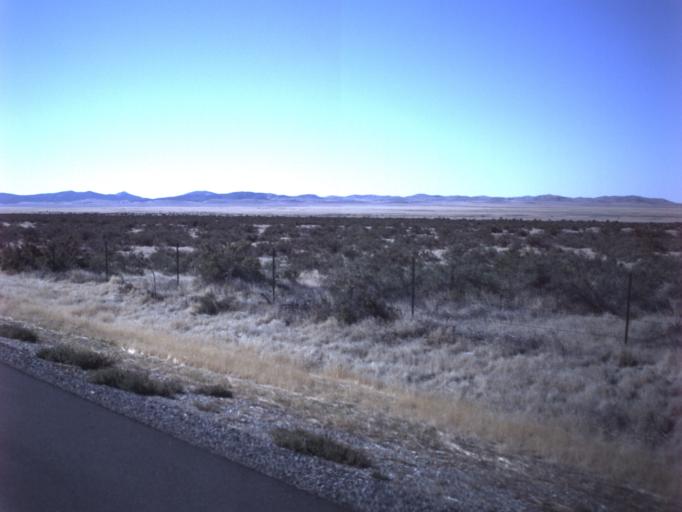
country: US
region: Utah
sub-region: Tooele County
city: Grantsville
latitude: 40.3573
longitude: -112.7457
